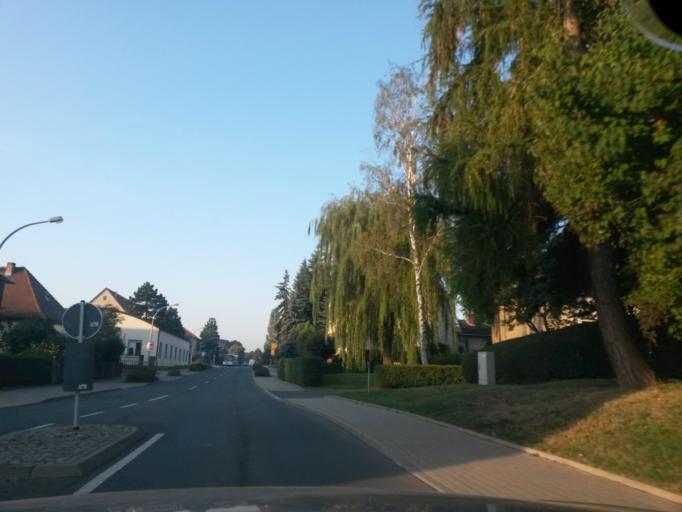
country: DE
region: Thuringia
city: Hermsdorf
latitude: 50.8886
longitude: 11.8529
